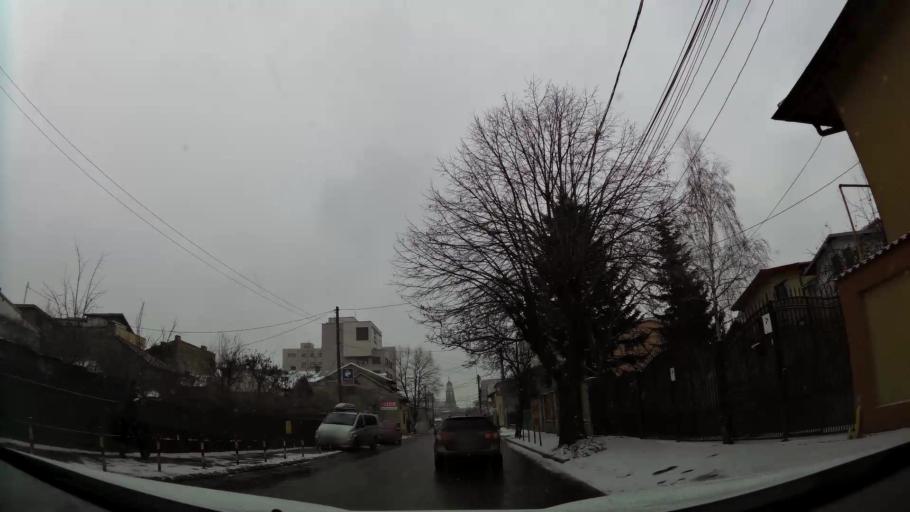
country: RO
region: Prahova
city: Ploiesti
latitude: 44.9476
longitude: 26.0191
